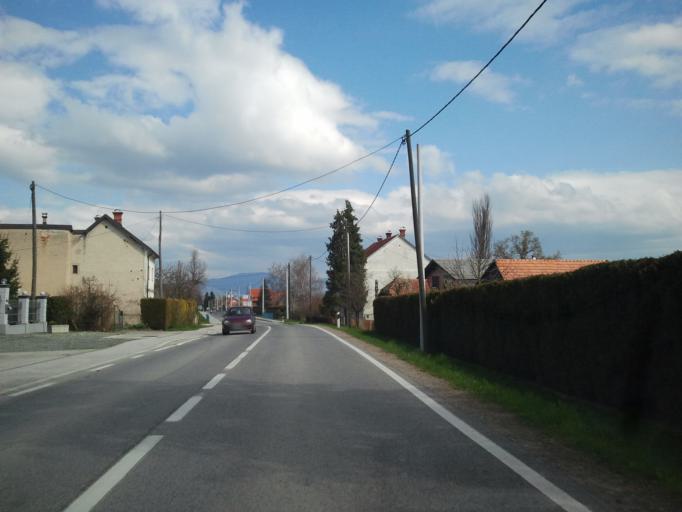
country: HR
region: Zagrebacka
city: Jastrebarsko
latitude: 45.5976
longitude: 15.5987
